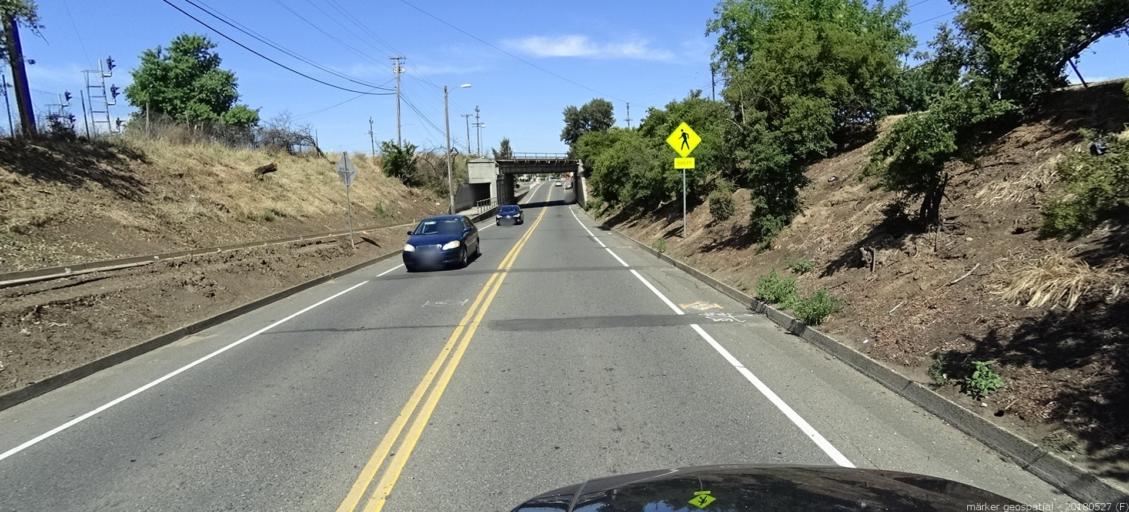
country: US
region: California
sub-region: Sacramento County
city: Rosemont
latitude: 38.5525
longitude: -121.4222
